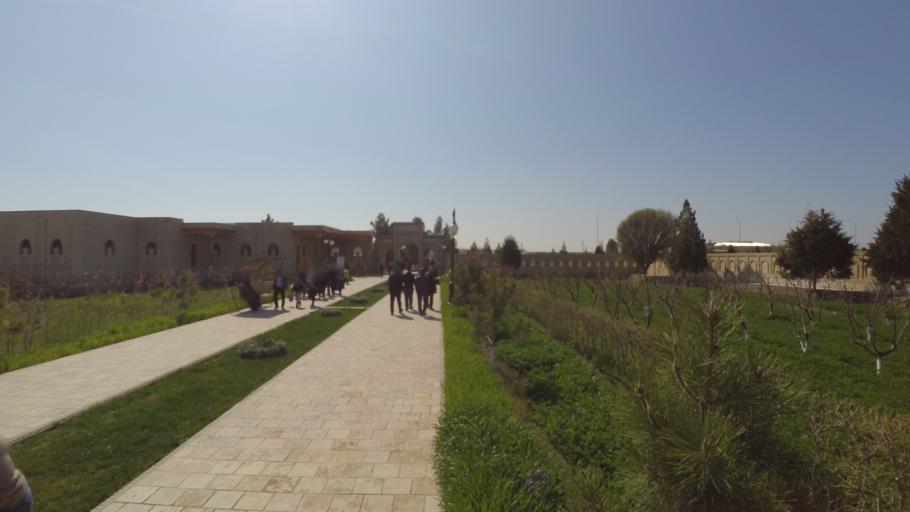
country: UZ
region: Bukhara
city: Kogon
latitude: 39.8010
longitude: 64.5387
